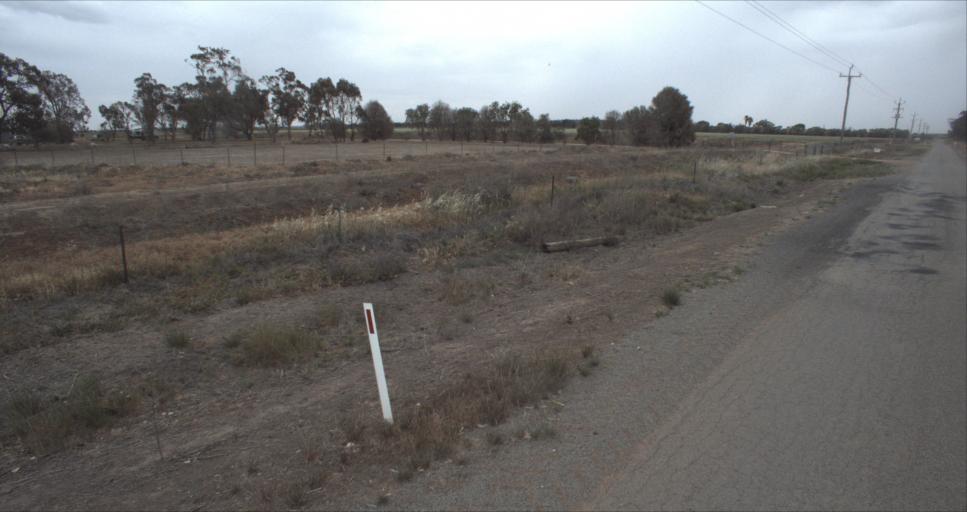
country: AU
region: New South Wales
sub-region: Leeton
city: Leeton
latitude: -34.4087
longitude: 146.3407
